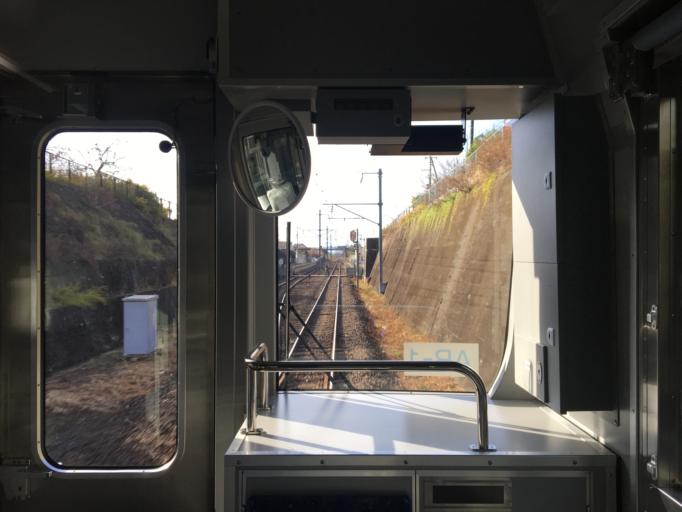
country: JP
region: Fukushima
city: Yanagawamachi-saiwaicho
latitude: 37.8753
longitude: 140.6281
